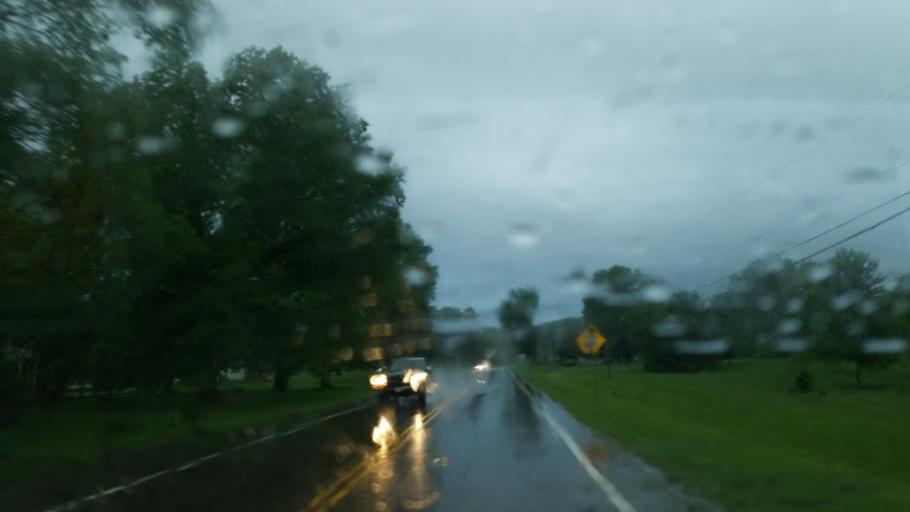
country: US
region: Ohio
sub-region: Knox County
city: Gambier
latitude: 40.3851
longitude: -82.4390
